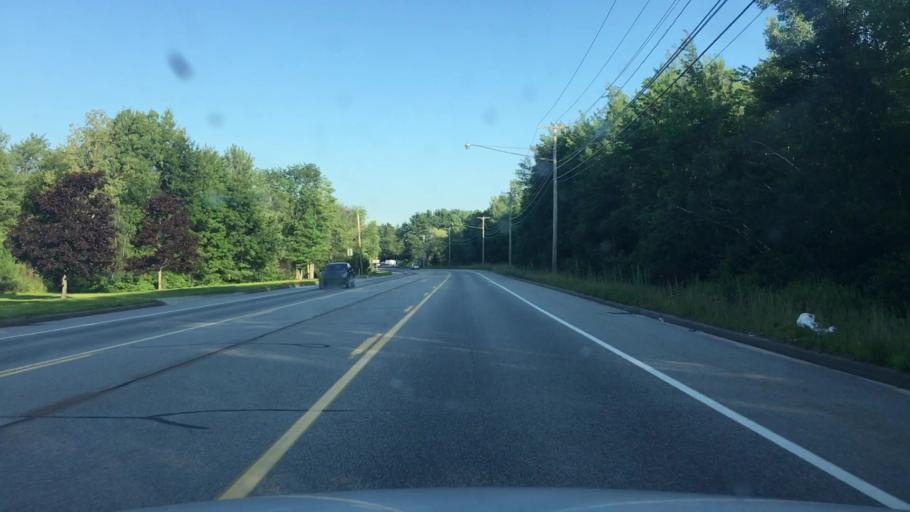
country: US
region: Maine
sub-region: Androscoggin County
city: Lisbon
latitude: 44.0538
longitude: -70.1383
